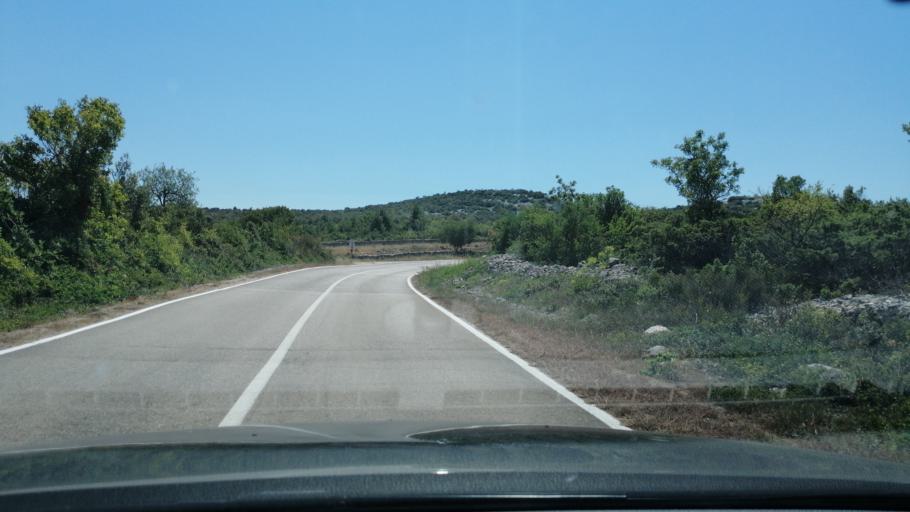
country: HR
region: Sibensko-Kniniska
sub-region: Grad Sibenik
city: Pirovac
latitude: 43.8599
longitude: 15.6922
